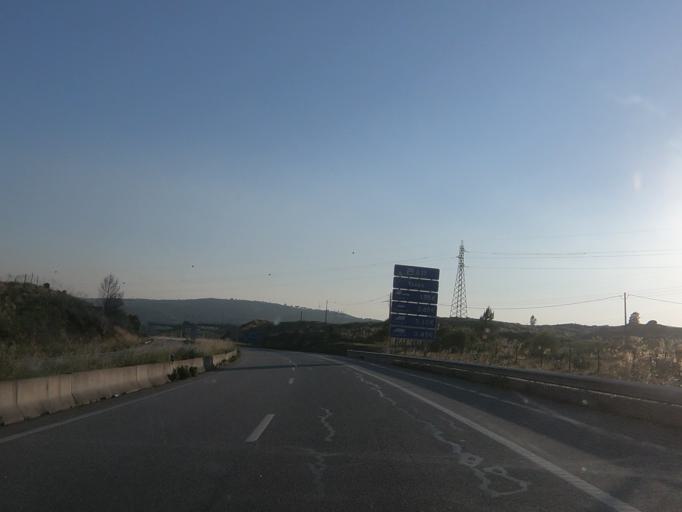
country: PT
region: Guarda
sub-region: Celorico da Beira
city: Celorico da Beira
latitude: 40.6306
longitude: -7.4190
